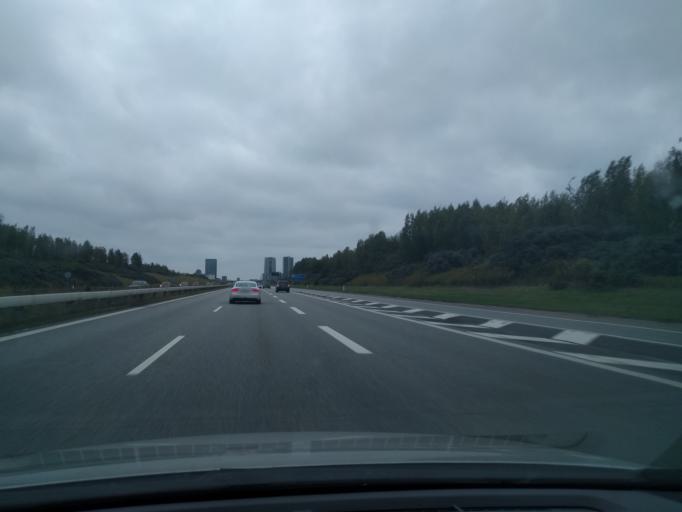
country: DK
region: Capital Region
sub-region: Tarnby Kommune
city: Tarnby
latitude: 55.6280
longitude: 12.5547
